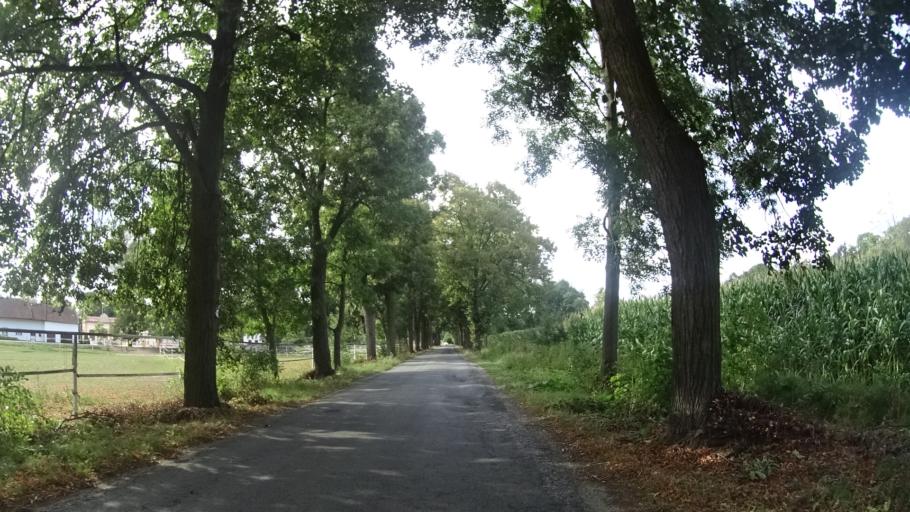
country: CZ
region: Olomoucky
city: Dubicko
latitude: 49.8033
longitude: 16.9444
